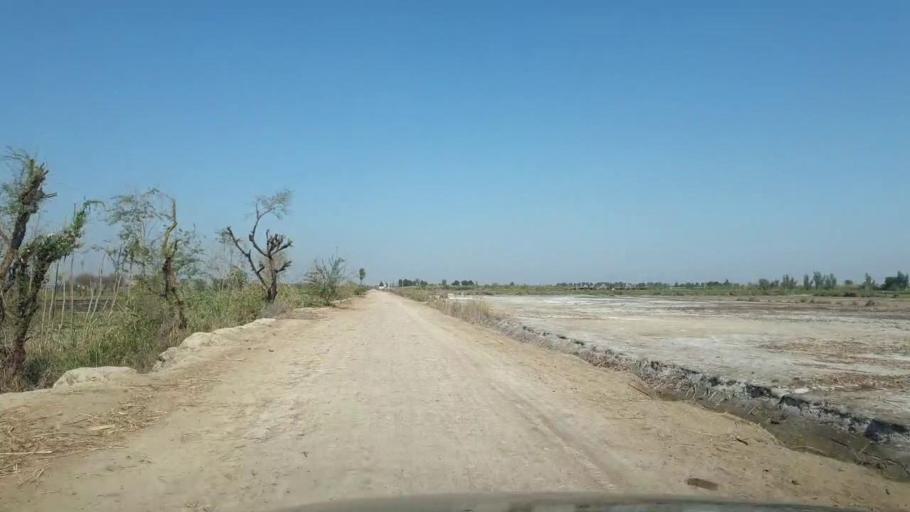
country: PK
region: Sindh
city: Mirpur Khas
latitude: 25.5932
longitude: 69.0556
